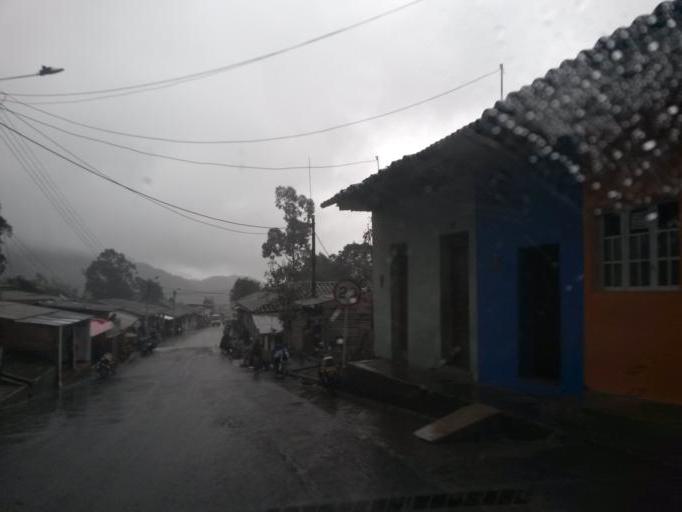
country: CO
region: Cauca
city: Paispamba
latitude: 2.3411
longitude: -76.4965
